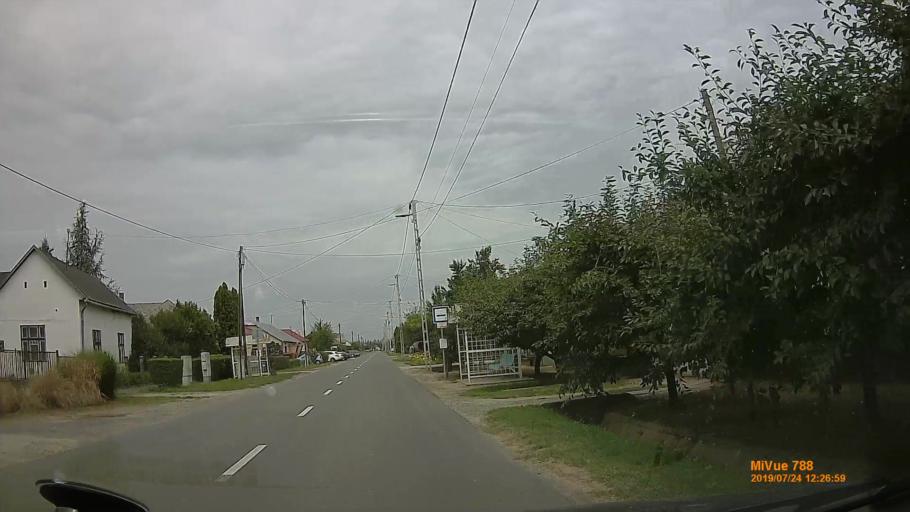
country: HU
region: Szabolcs-Szatmar-Bereg
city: Vasarosnameny
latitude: 48.1324
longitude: 22.3435
